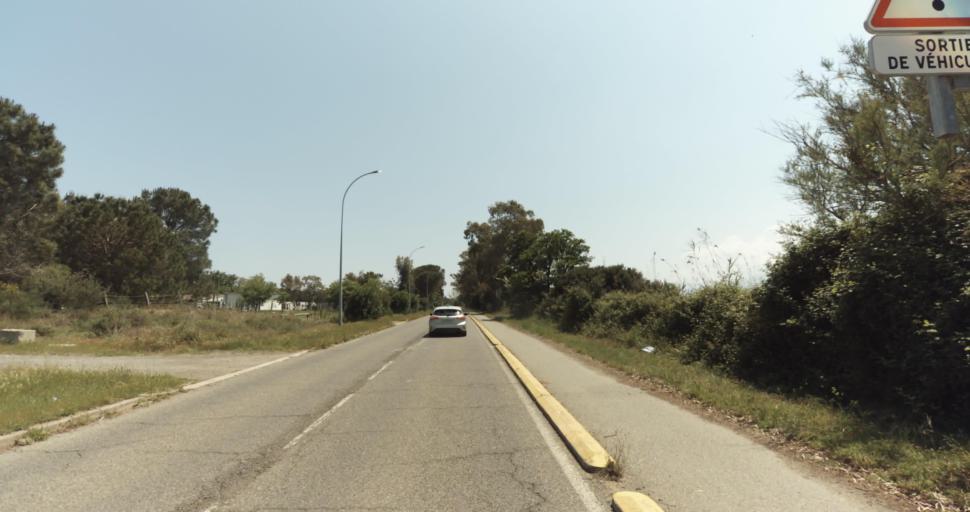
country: FR
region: Corsica
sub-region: Departement de la Haute-Corse
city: Biguglia
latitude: 42.6472
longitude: 9.4537
